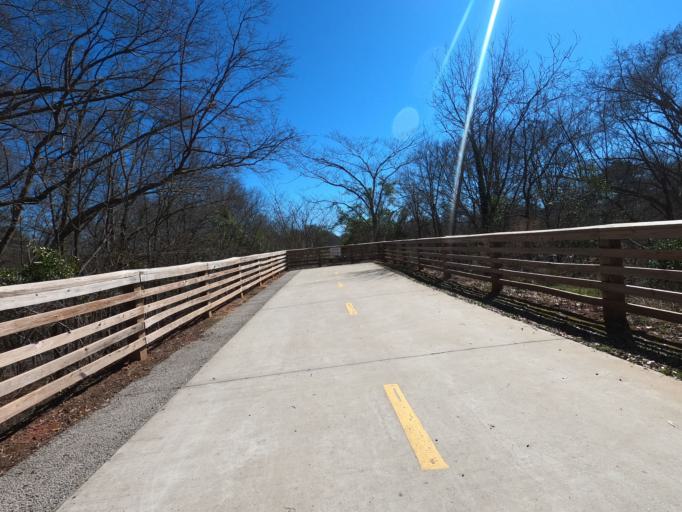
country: US
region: Georgia
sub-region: Clarke County
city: Athens
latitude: 33.9554
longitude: -83.3653
